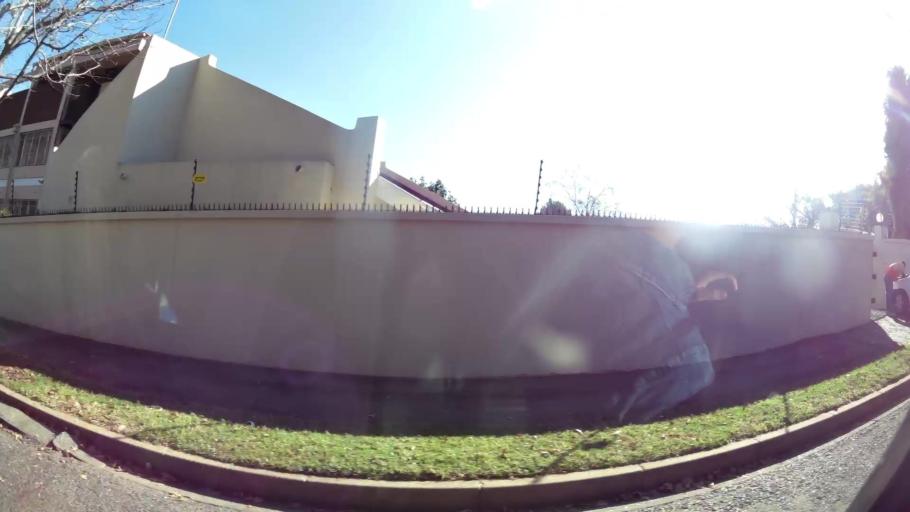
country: ZA
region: Gauteng
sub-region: City of Johannesburg Metropolitan Municipality
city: Johannesburg
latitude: -26.1237
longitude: 28.0224
